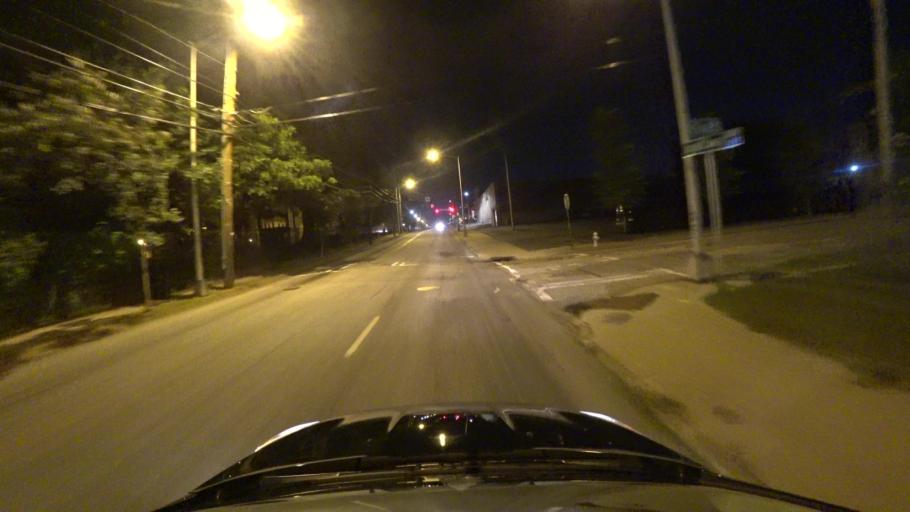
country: US
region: Georgia
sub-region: Fulton County
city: Atlanta
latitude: 33.7365
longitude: -84.4177
